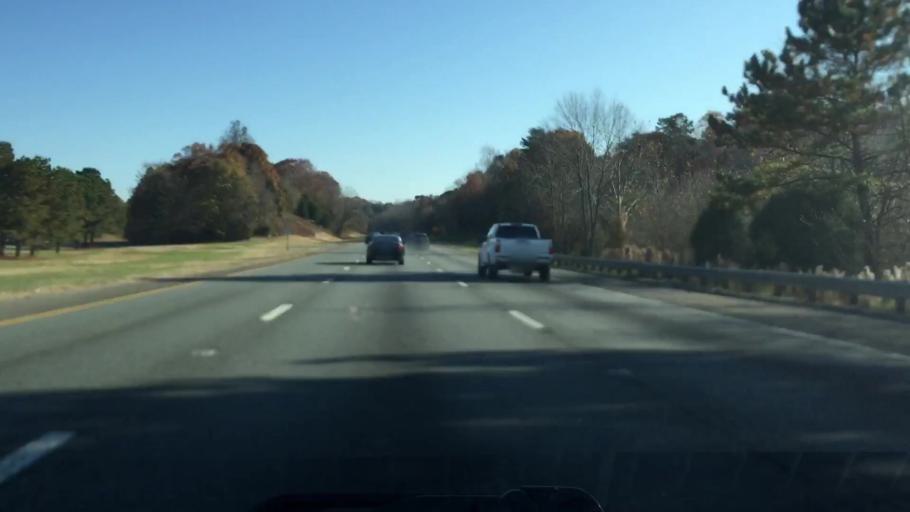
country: US
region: North Carolina
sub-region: Davidson County
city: Lexington
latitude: 35.7869
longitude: -80.2346
